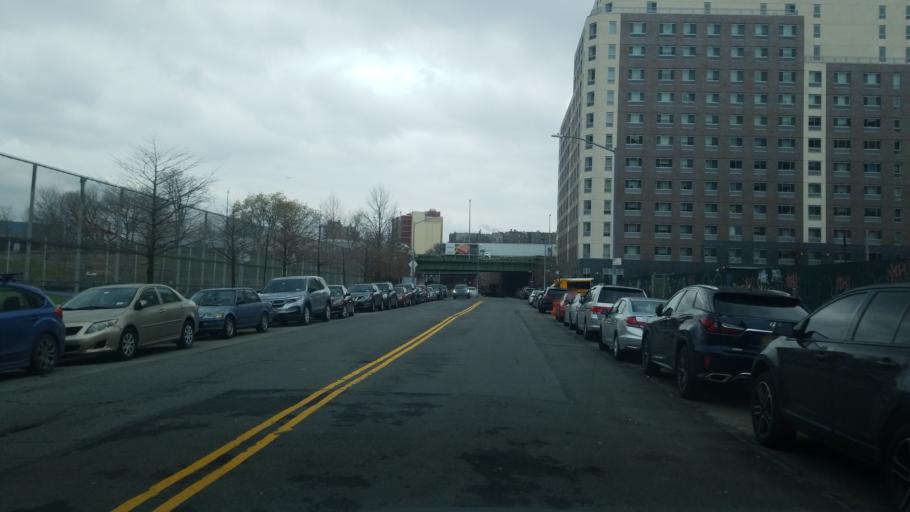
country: US
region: New York
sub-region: Bronx
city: The Bronx
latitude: 40.8394
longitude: -73.8804
